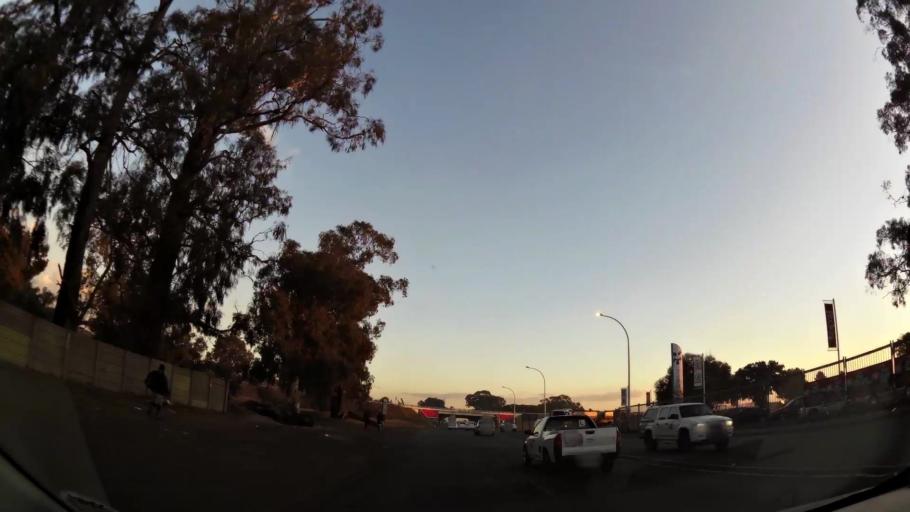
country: ZA
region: Mpumalanga
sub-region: Nkangala District Municipality
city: Witbank
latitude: -25.8834
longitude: 29.2079
